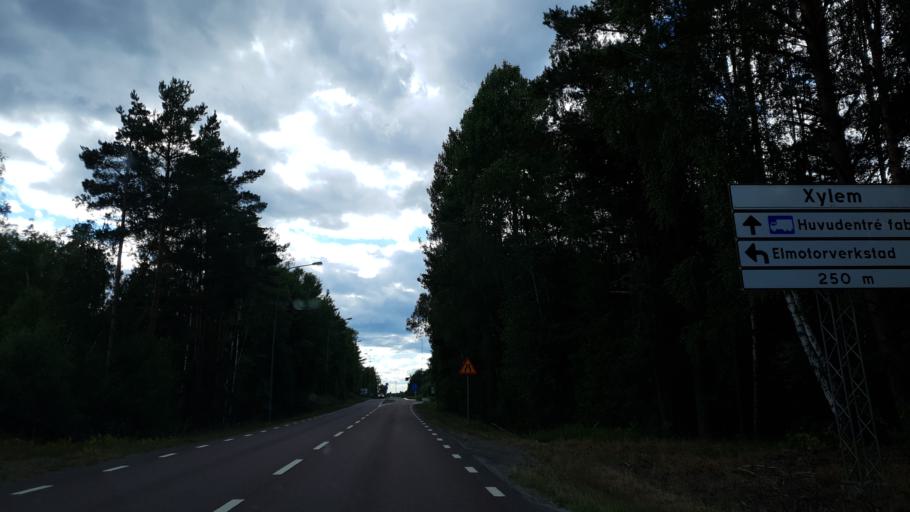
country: SE
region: Kalmar
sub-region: Emmaboda Kommun
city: Emmaboda
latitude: 56.6236
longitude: 15.5730
